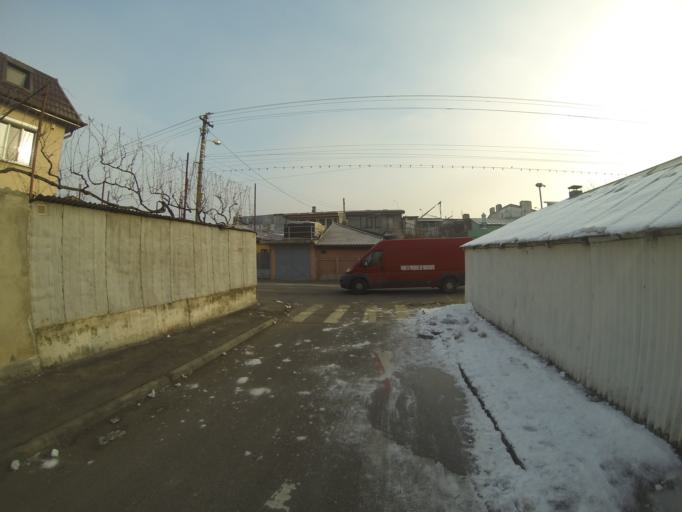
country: RO
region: Bucuresti
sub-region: Municipiul Bucuresti
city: Bucuresti
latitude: 44.3982
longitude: 26.0795
